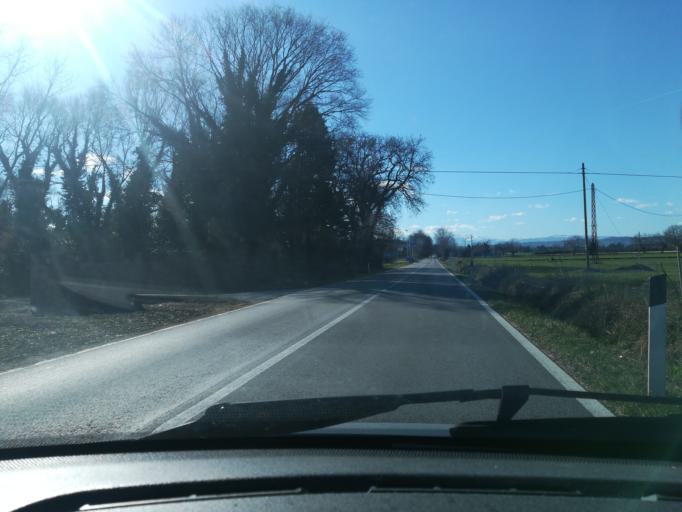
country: IT
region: The Marches
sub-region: Provincia di Macerata
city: Villa Potenza
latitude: 43.3397
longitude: 13.4300
